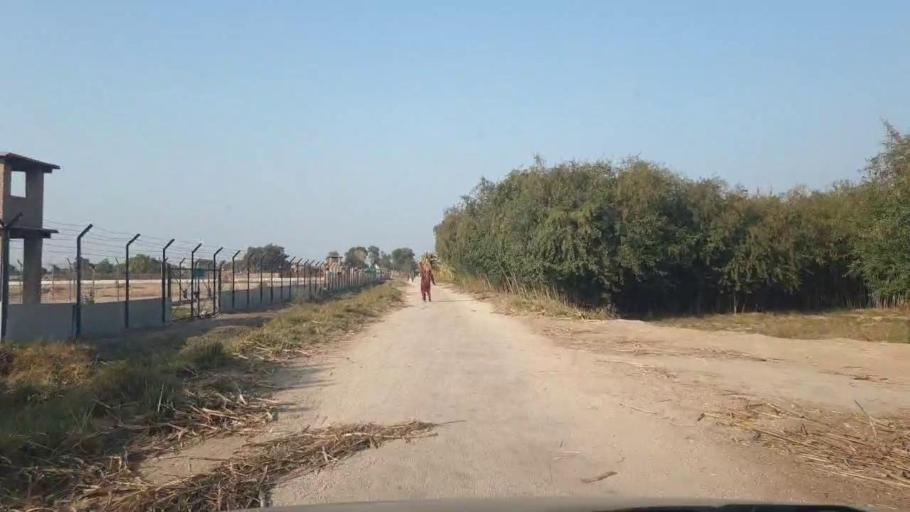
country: PK
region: Sindh
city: Bhit Shah
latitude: 25.8302
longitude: 68.5200
